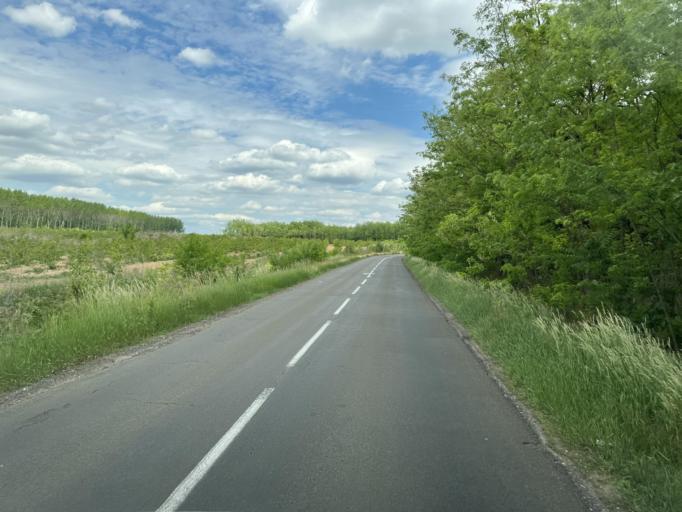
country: HU
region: Pest
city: Tapioszecso
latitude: 47.4713
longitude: 19.6209
